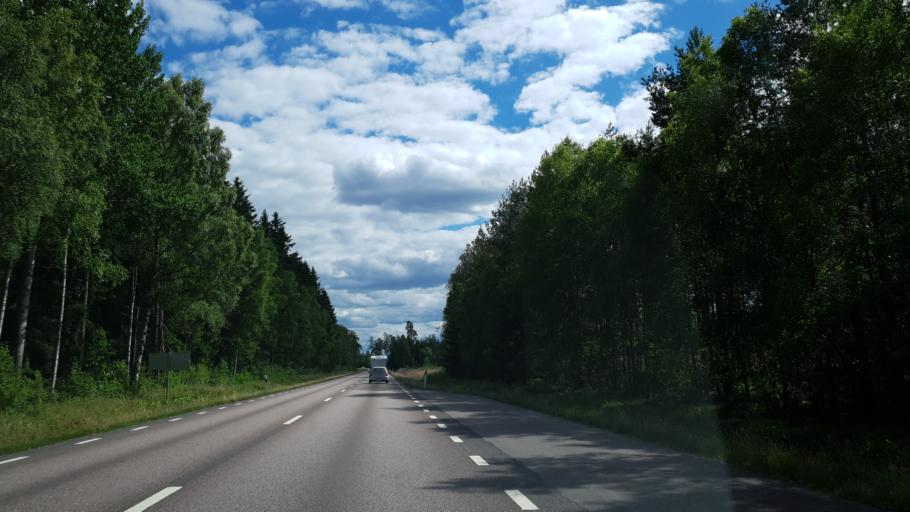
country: SE
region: Kronoberg
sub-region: Lessebo Kommun
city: Lessebo
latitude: 56.8388
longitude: 15.3916
